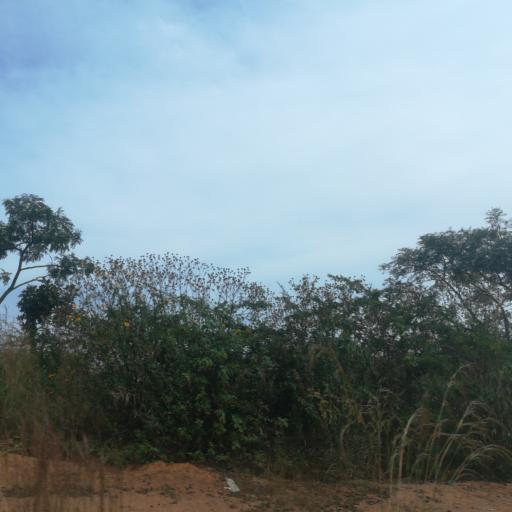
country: NG
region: Plateau
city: Jos
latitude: 9.8892
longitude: 8.8401
